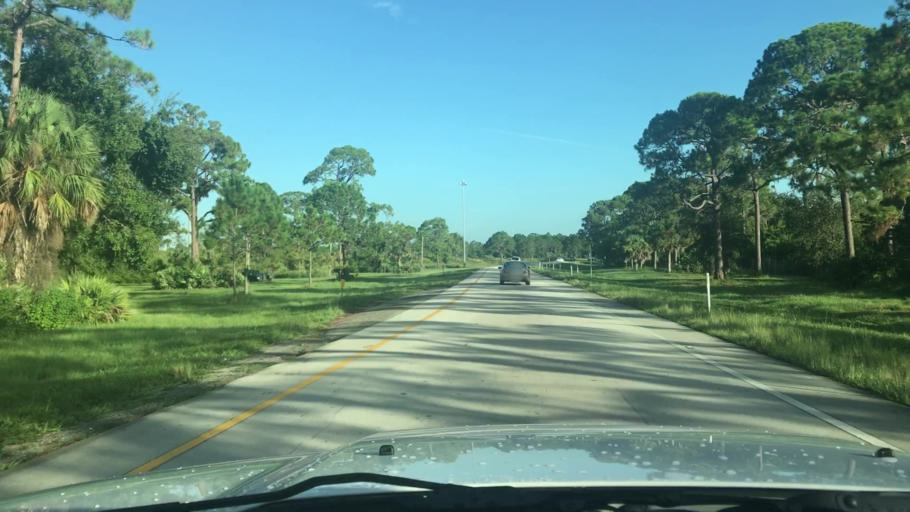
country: US
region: Florida
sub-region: Martin County
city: Palm City
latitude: 27.1628
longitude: -80.3881
